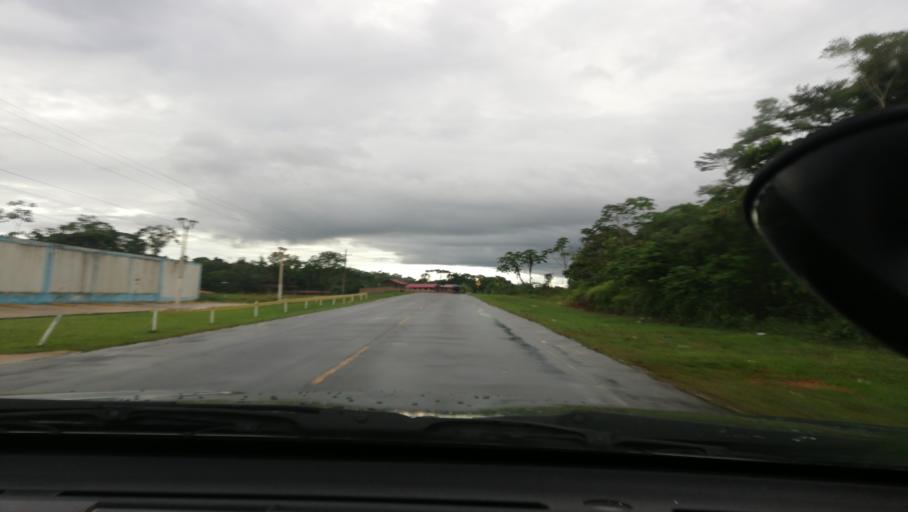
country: PE
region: Loreto
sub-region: Provincia de Maynas
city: Iquitos
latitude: -3.9145
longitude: -73.3643
